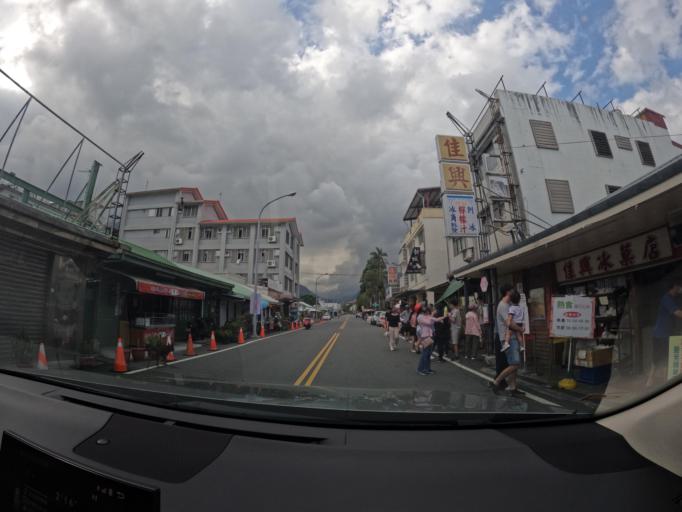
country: TW
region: Taiwan
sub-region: Hualien
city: Hualian
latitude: 24.1265
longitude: 121.6518
